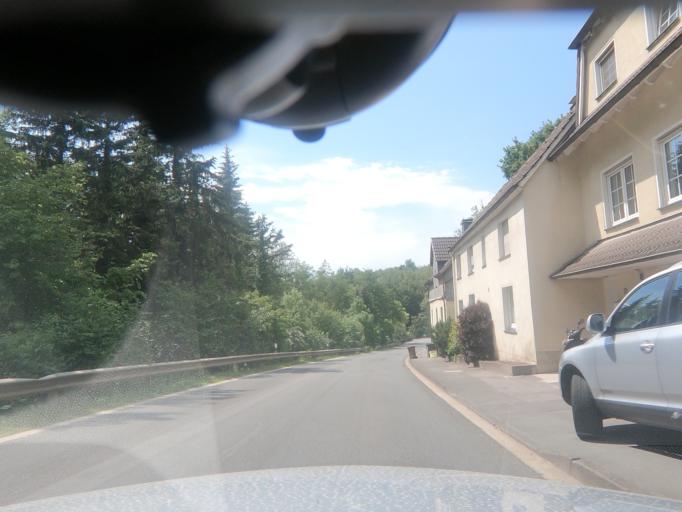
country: DE
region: North Rhine-Westphalia
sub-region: Regierungsbezirk Arnsberg
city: Sundern
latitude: 51.3197
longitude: 8.0548
